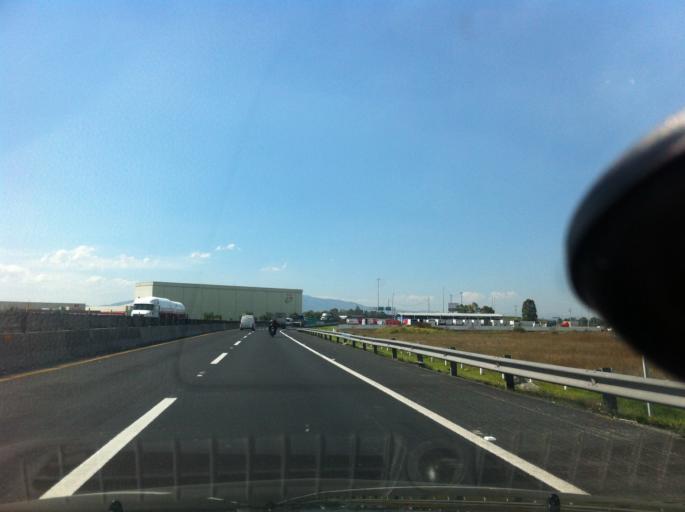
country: MX
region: Mexico
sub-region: Cuautitlan
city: La Providencia
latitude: 19.7492
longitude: -99.1224
